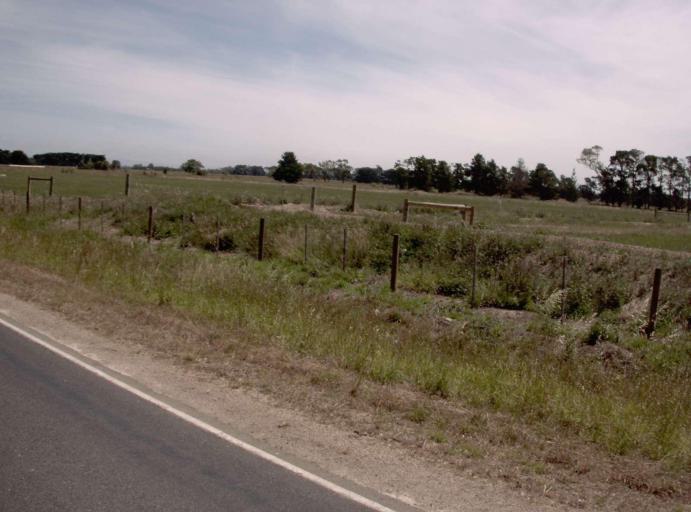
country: AU
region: Victoria
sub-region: Wellington
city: Heyfield
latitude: -38.0377
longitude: 146.8778
